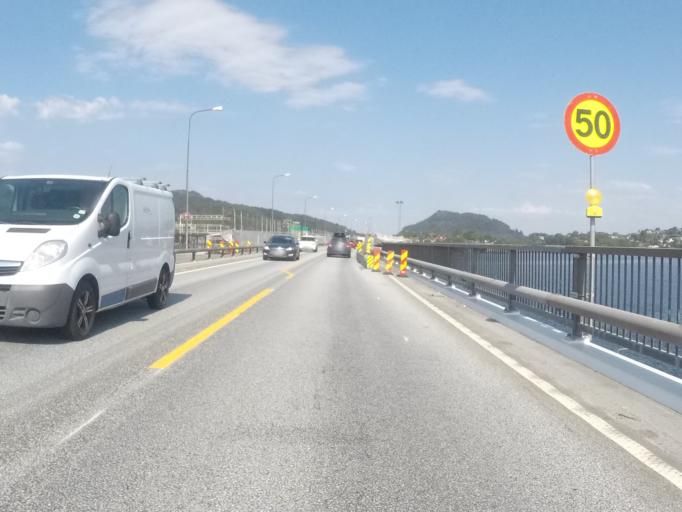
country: NO
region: Hordaland
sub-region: Meland
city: Frekhaug
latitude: 60.5236
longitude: 5.2650
